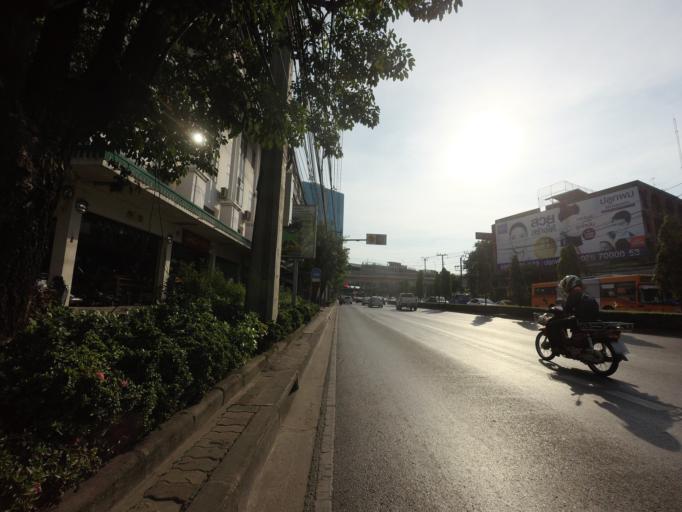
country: TH
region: Bangkok
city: Watthana
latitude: 13.7442
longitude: 100.6025
